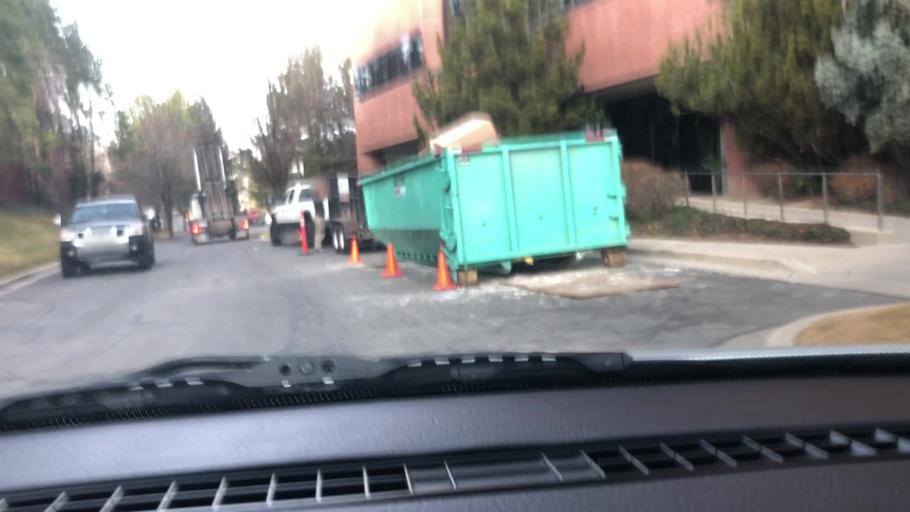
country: US
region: Utah
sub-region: Salt Lake County
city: Millcreek
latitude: 40.6840
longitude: -111.8697
